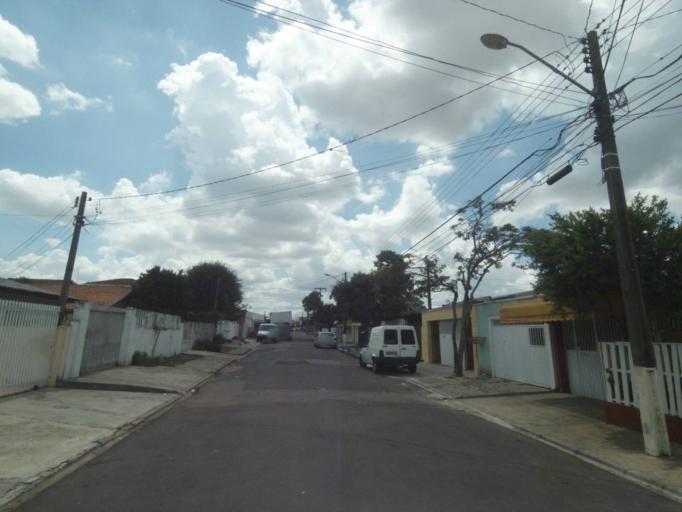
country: BR
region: Parana
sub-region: Sao Jose Dos Pinhais
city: Sao Jose dos Pinhais
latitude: -25.5390
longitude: -49.2709
